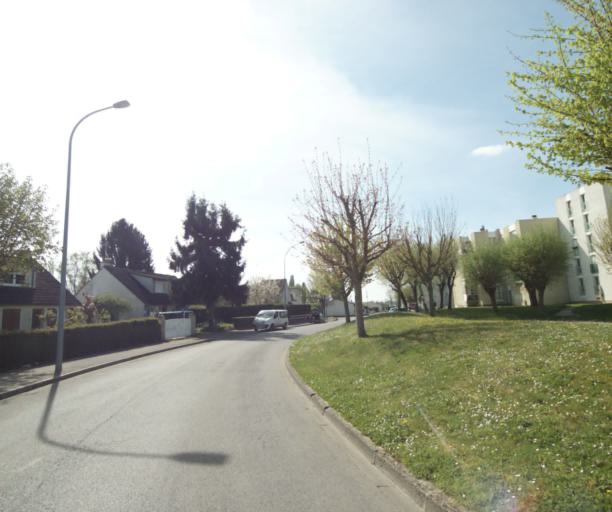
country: FR
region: Ile-de-France
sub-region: Departement de Seine-et-Marne
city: Nangis
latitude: 48.5529
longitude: 3.0219
